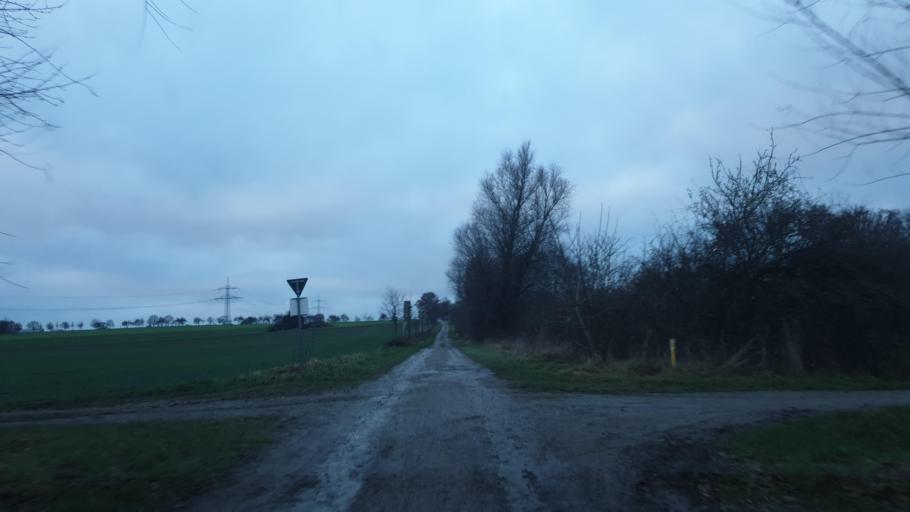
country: DE
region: North Rhine-Westphalia
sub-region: Regierungsbezirk Detmold
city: Hiddenhausen
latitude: 52.1412
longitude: 8.6324
